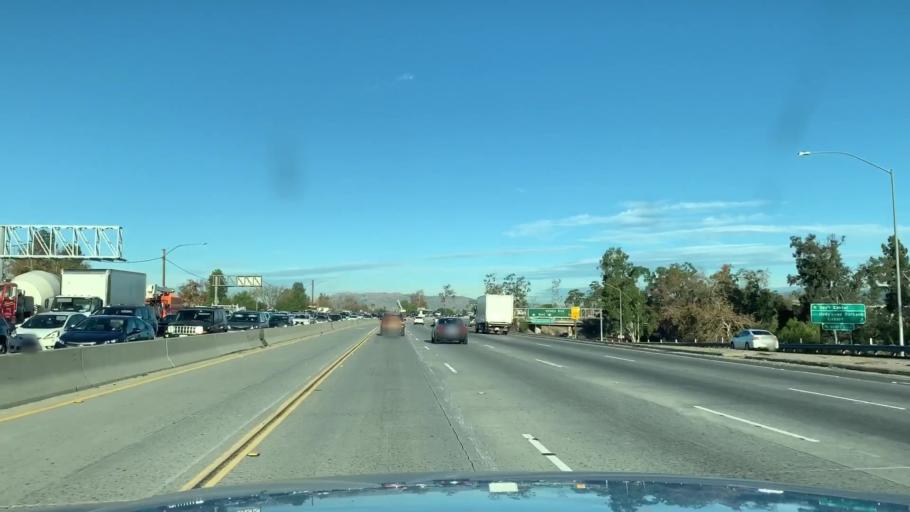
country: US
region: California
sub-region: Los Angeles County
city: North Hollywood
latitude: 34.1829
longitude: -118.3983
